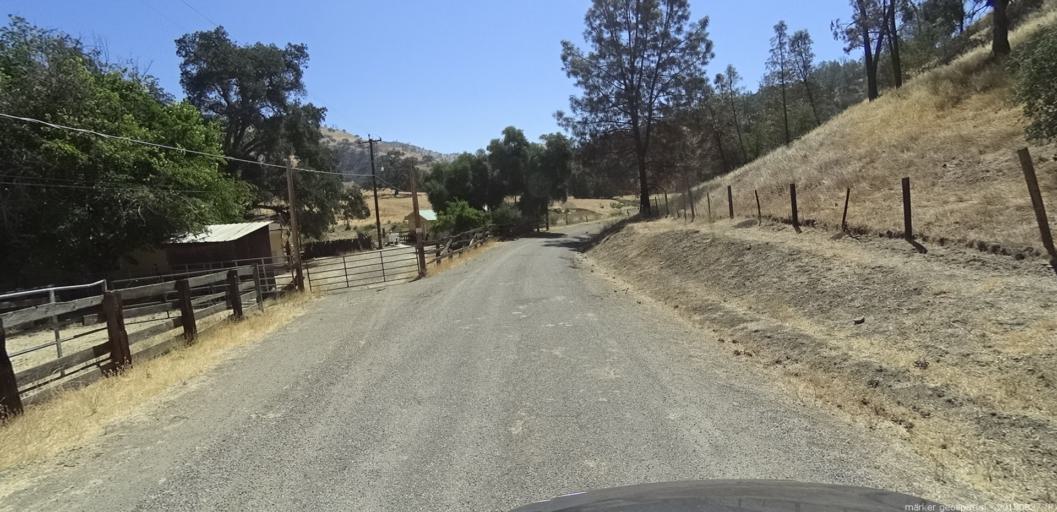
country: US
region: California
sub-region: Monterey County
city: King City
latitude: 36.2860
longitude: -120.8579
